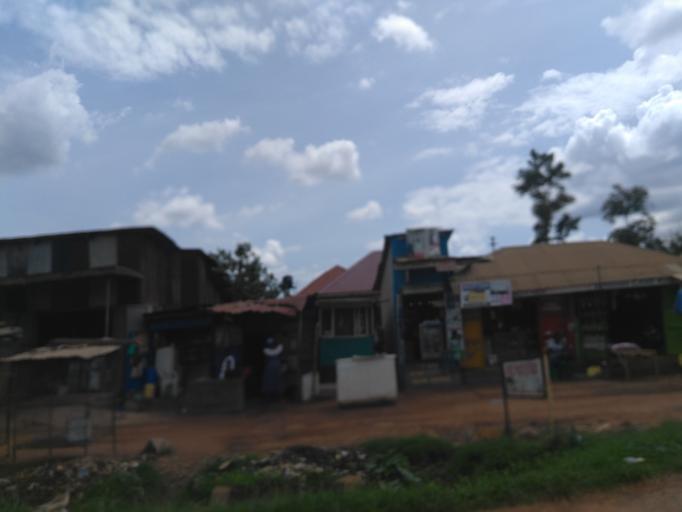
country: UG
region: Central Region
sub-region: Wakiso District
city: Kireka
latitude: 0.4271
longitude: 32.5992
